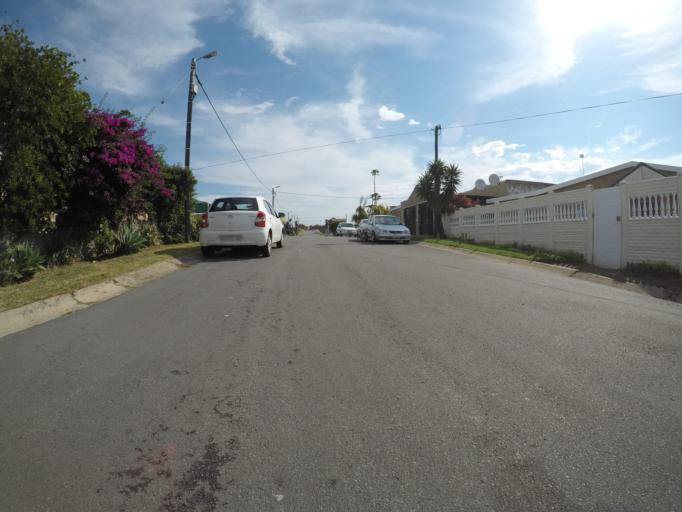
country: ZA
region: Eastern Cape
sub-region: Buffalo City Metropolitan Municipality
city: East London
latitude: -33.0217
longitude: 27.8816
